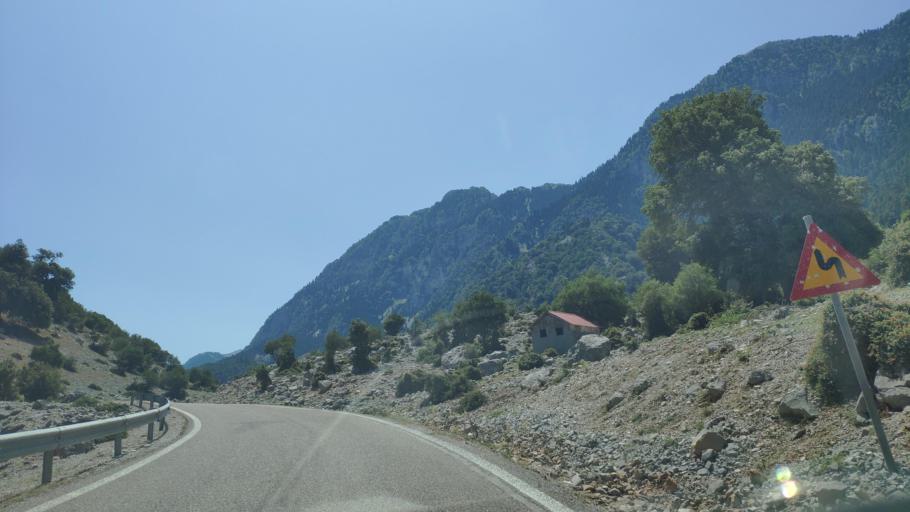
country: GR
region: West Greece
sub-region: Nomos Aitolias kai Akarnanias
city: Krikellos
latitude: 39.0109
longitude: 21.3586
